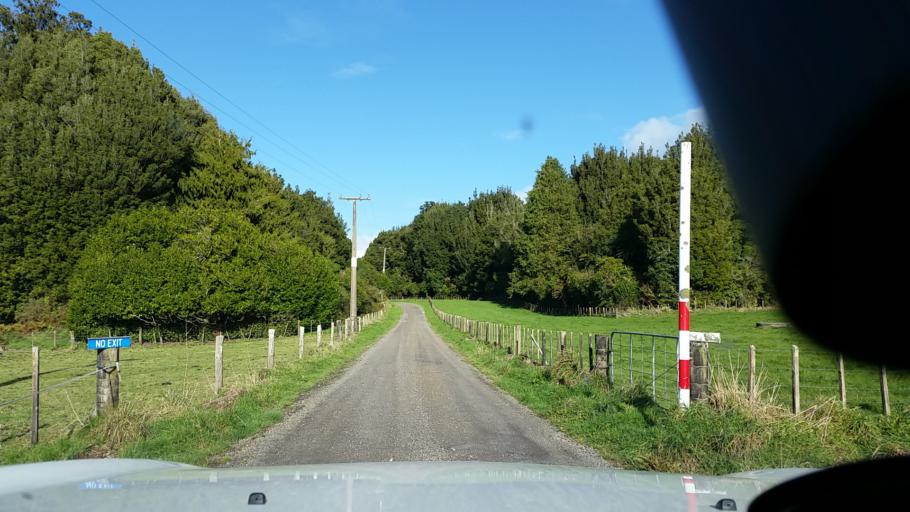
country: NZ
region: Bay of Plenty
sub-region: Rotorua District
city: Rotorua
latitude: -38.1007
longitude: 176.0675
